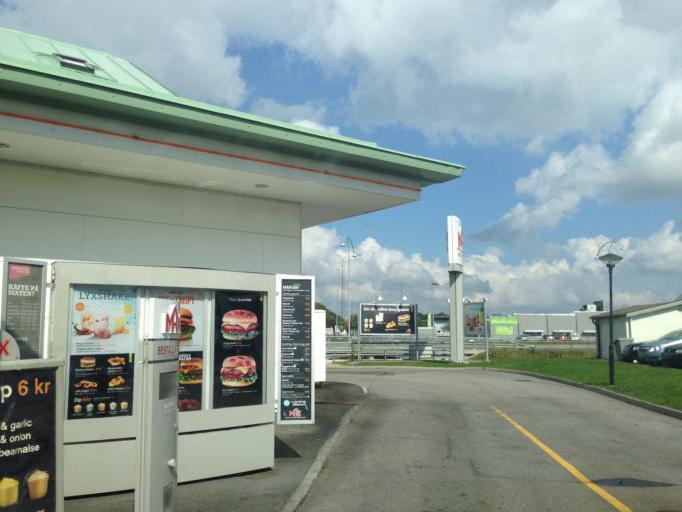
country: SE
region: Skane
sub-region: Lunds Kommun
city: Lund
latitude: 55.7159
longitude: 13.1563
